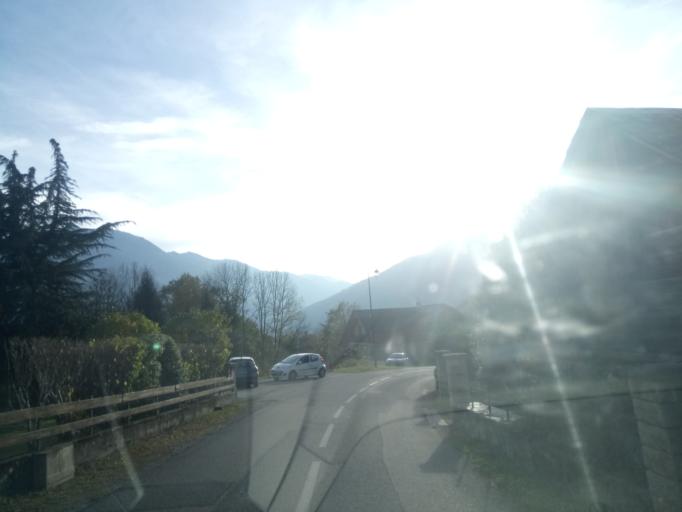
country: FR
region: Rhone-Alpes
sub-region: Departement de la Savoie
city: La Chambre
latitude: 45.3716
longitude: 6.3131
